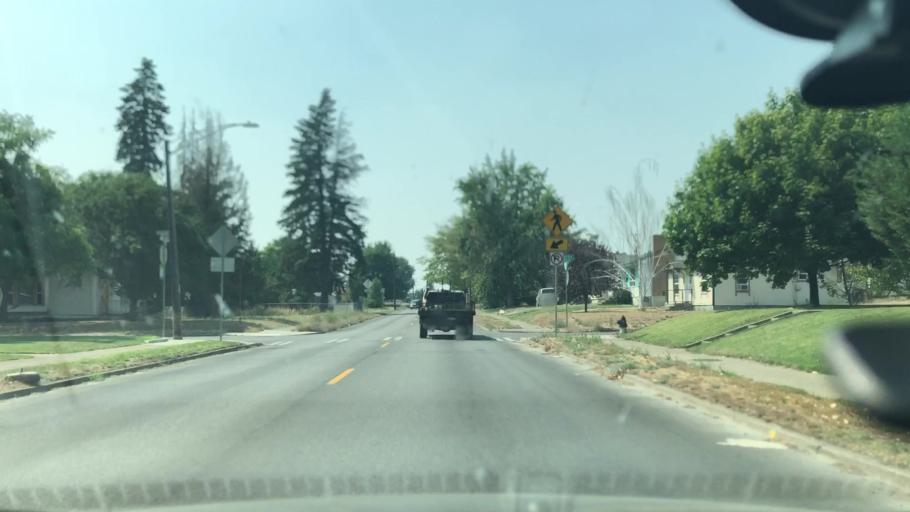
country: US
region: Washington
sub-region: Spokane County
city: Millwood
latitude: 47.6858
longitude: -117.3513
